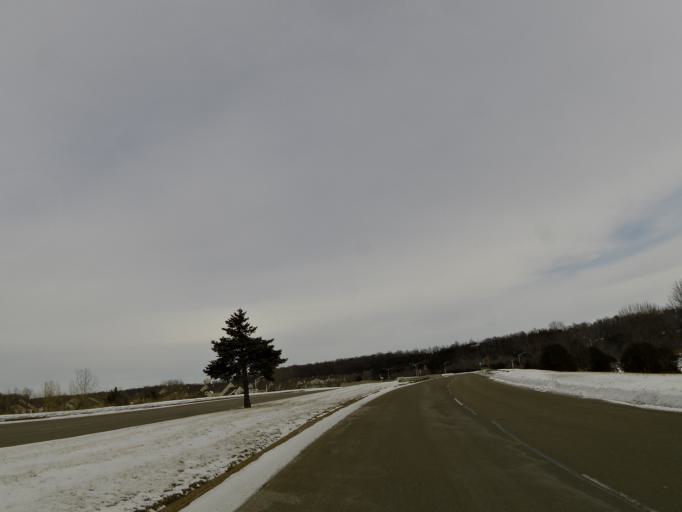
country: US
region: Minnesota
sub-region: Washington County
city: Lakeland
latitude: 44.9486
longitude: -92.7286
